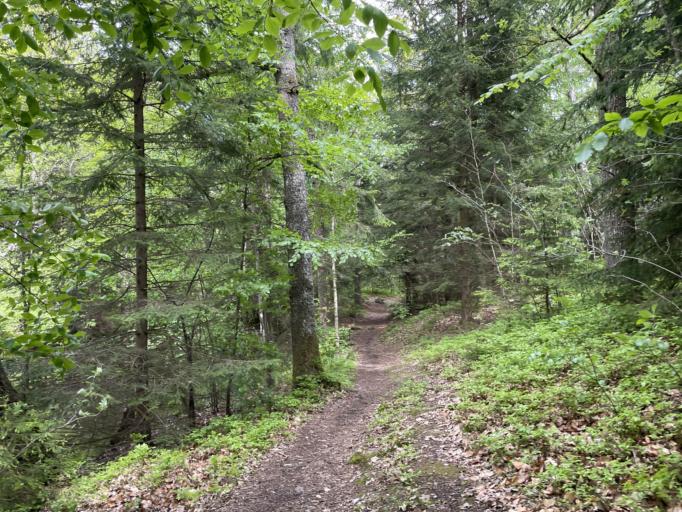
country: SE
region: Skane
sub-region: Klippans Kommun
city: Klippan
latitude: 56.1599
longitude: 13.1642
